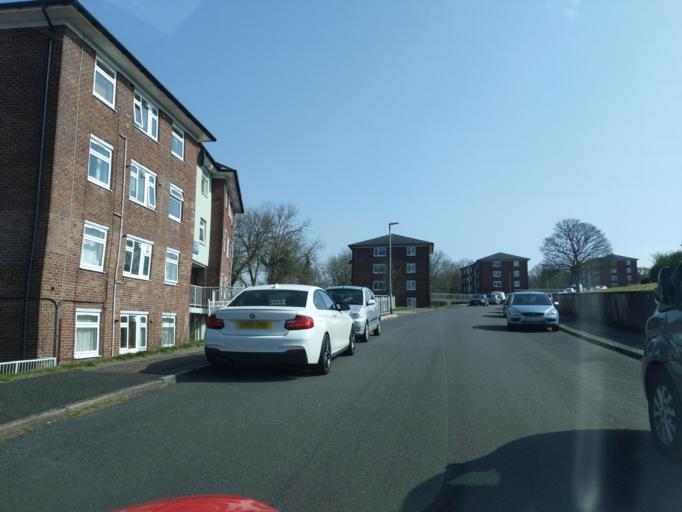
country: GB
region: England
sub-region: Plymouth
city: Plymouth
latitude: 50.4316
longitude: -4.1310
